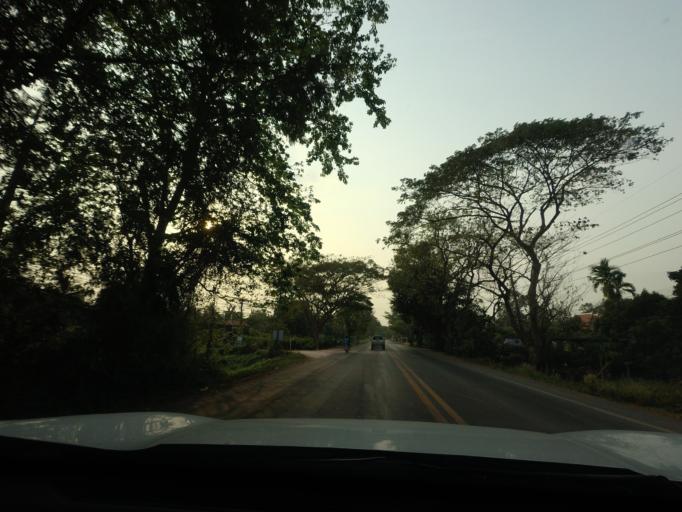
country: TH
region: Nakhon Nayok
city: Pak Phli
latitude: 14.1500
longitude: 101.3294
